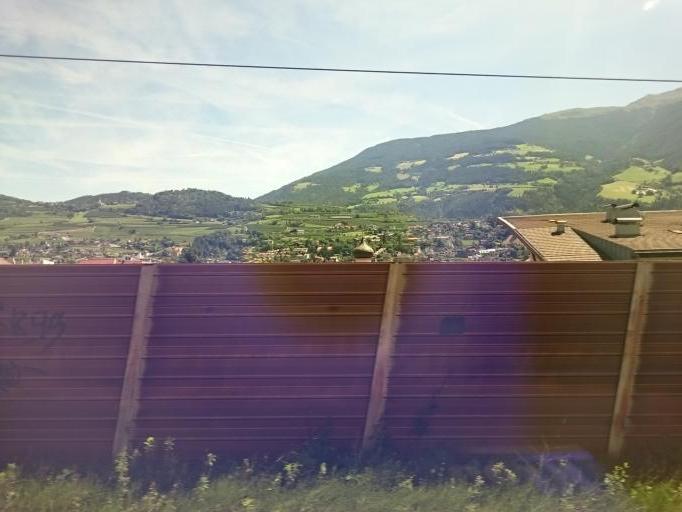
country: IT
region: Trentino-Alto Adige
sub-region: Bolzano
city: Bressanone
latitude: 46.7184
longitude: 11.6484
